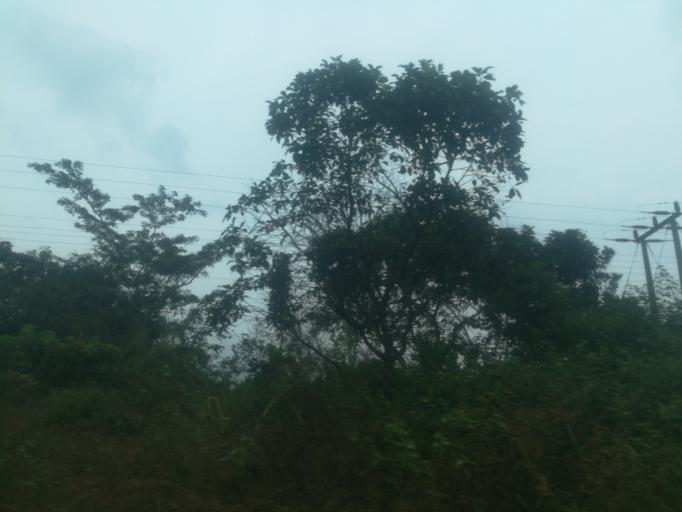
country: NG
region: Ogun
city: Ayetoro
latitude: 7.1084
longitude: 3.1369
